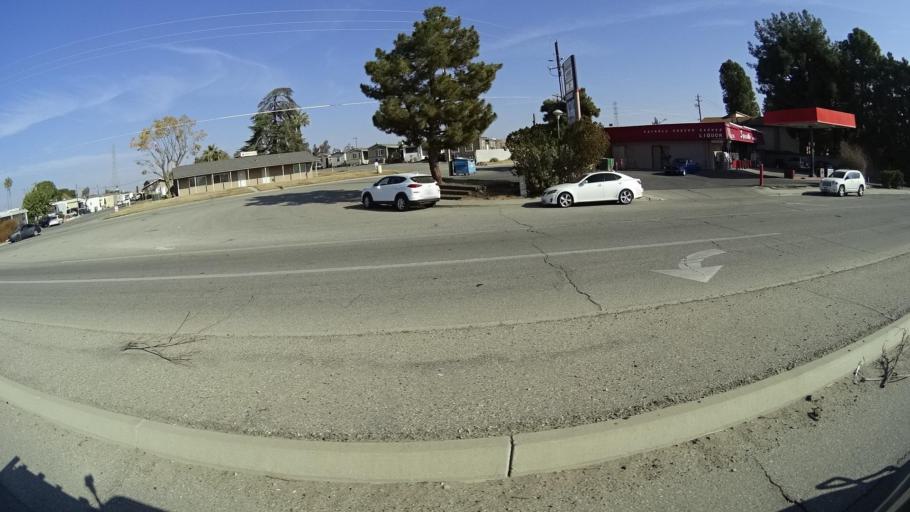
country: US
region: California
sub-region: Kern County
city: Oildale
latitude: 35.4482
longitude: -119.0305
